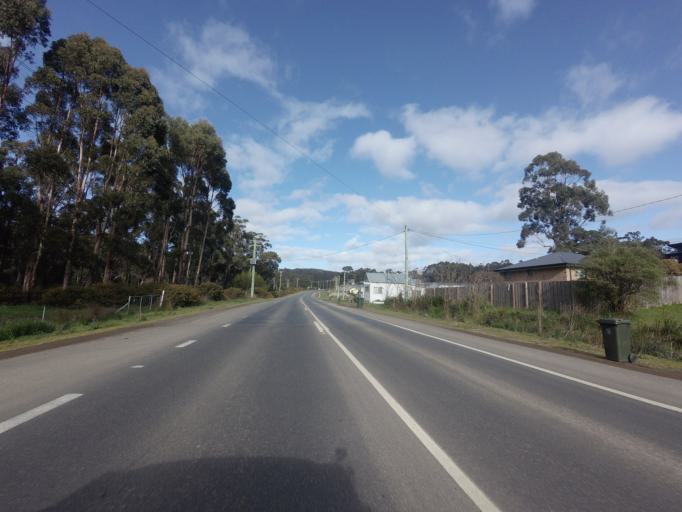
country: AU
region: Tasmania
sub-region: Huon Valley
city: Geeveston
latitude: -43.1637
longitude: 146.9483
